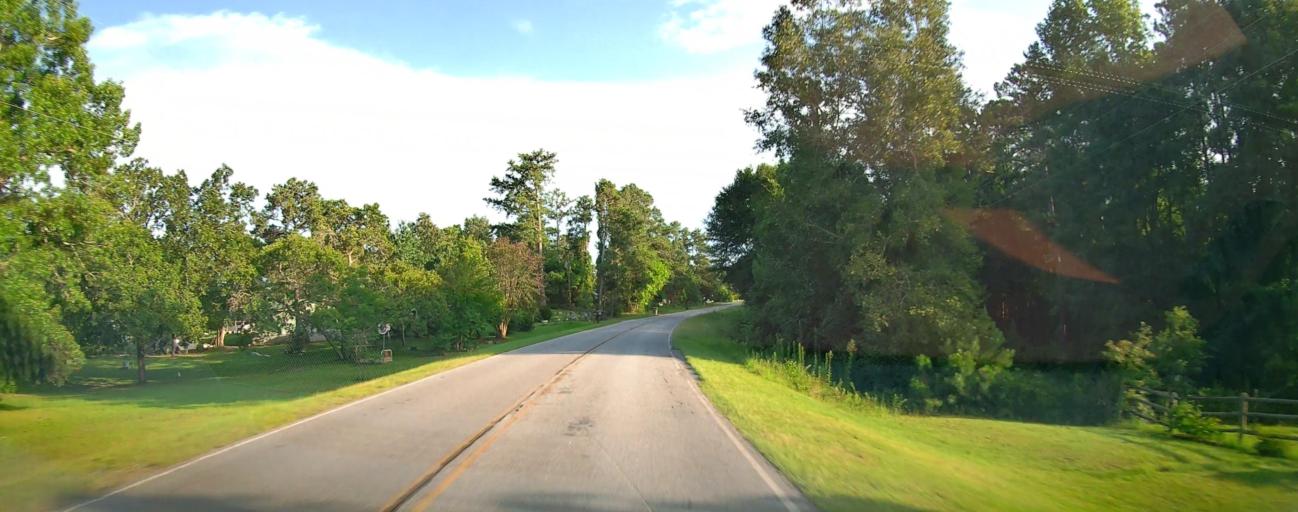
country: US
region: Georgia
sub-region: Peach County
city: Byron
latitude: 32.6996
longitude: -83.8501
